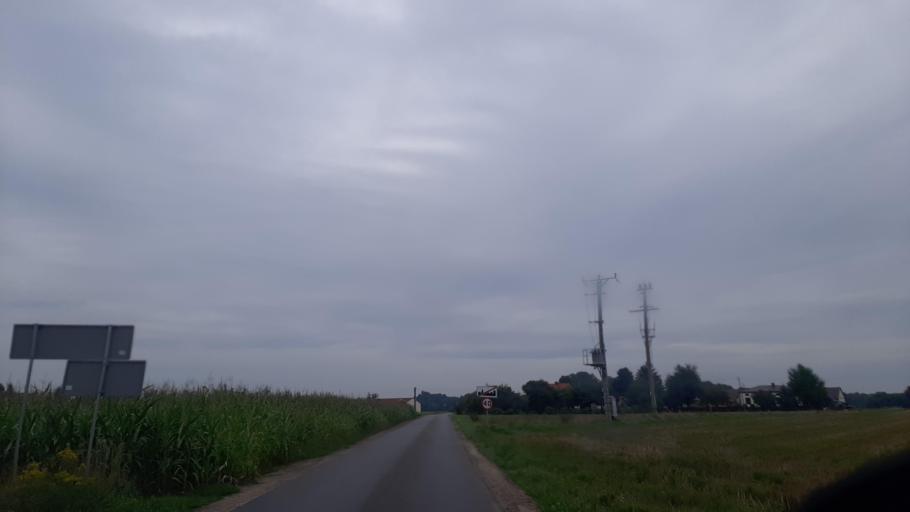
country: PL
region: Lublin Voivodeship
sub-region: Powiat lubartowski
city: Kamionka
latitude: 51.4684
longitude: 22.4196
